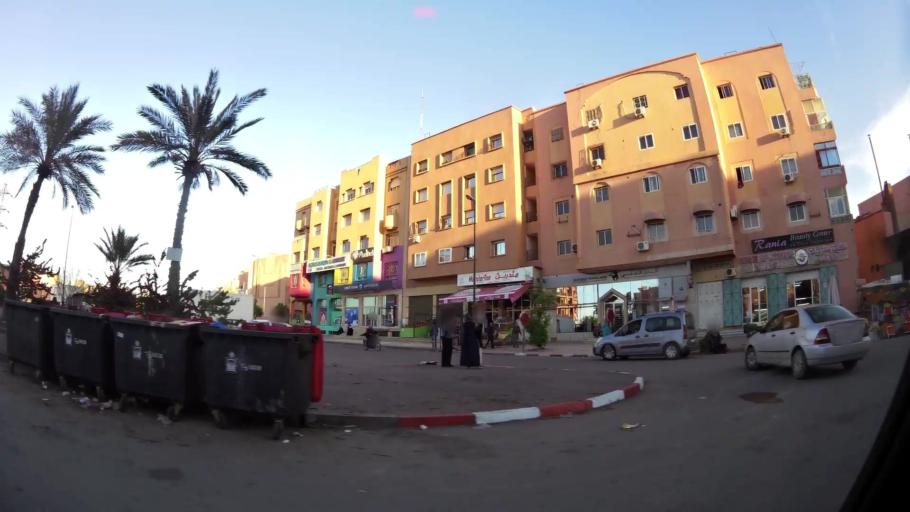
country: MA
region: Marrakech-Tensift-Al Haouz
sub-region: Marrakech
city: Marrakesh
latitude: 31.6236
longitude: -8.0300
